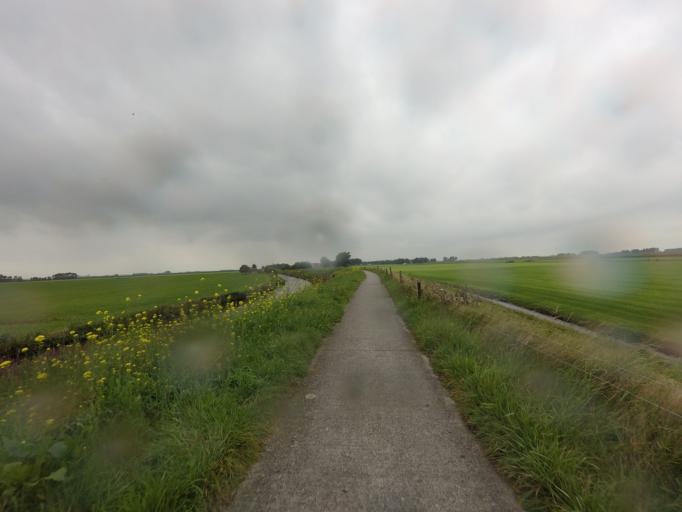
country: NL
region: Friesland
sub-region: Sudwest Fryslan
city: Workum
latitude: 52.9498
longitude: 5.4484
